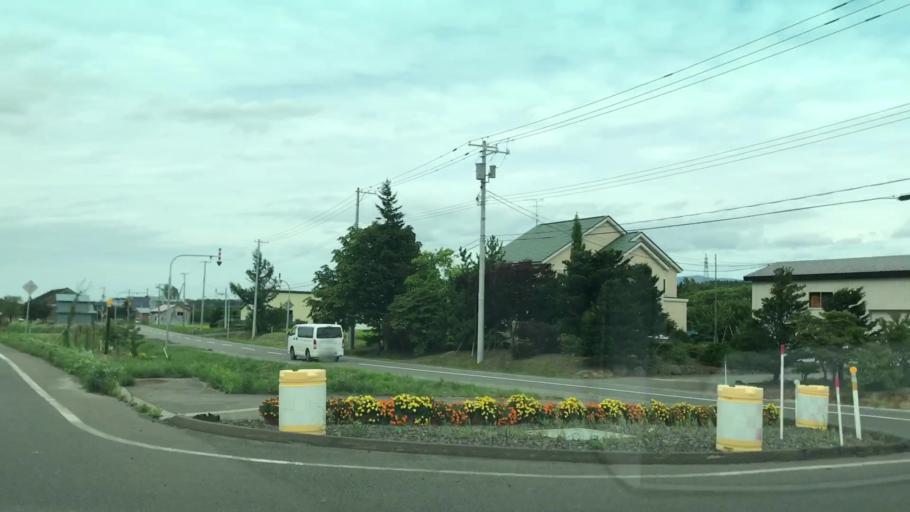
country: JP
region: Hokkaido
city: Iwanai
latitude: 42.9826
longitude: 140.6180
